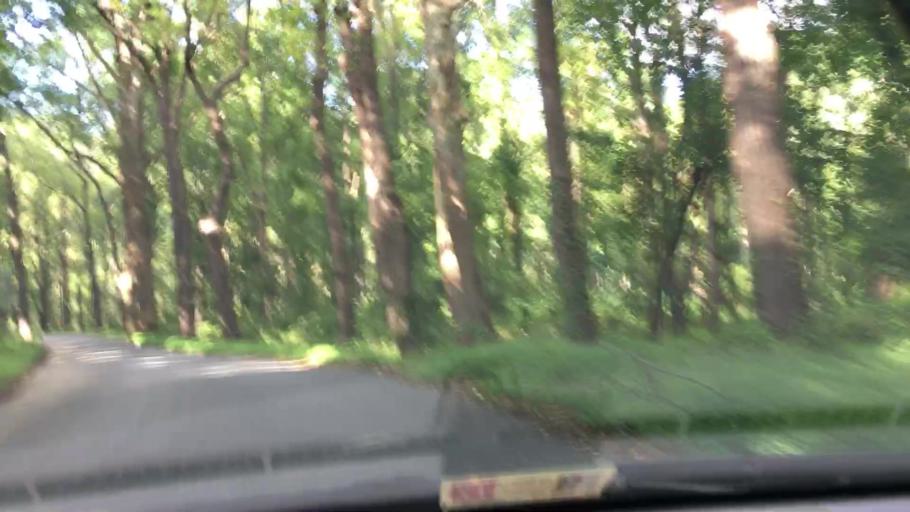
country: US
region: Maryland
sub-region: Montgomery County
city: Montgomery Village
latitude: 39.2113
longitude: -77.2051
